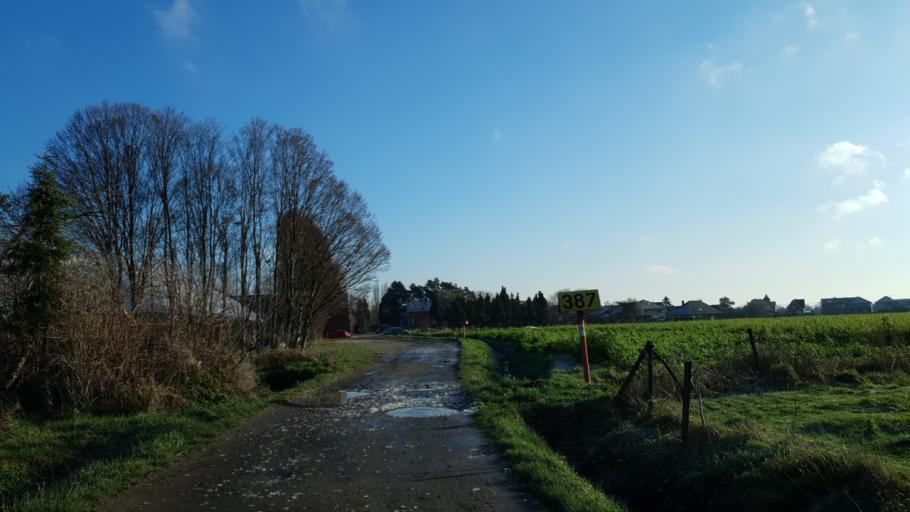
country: BE
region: Flanders
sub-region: Provincie Vlaams-Brabant
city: Herent
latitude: 50.9164
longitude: 4.6763
